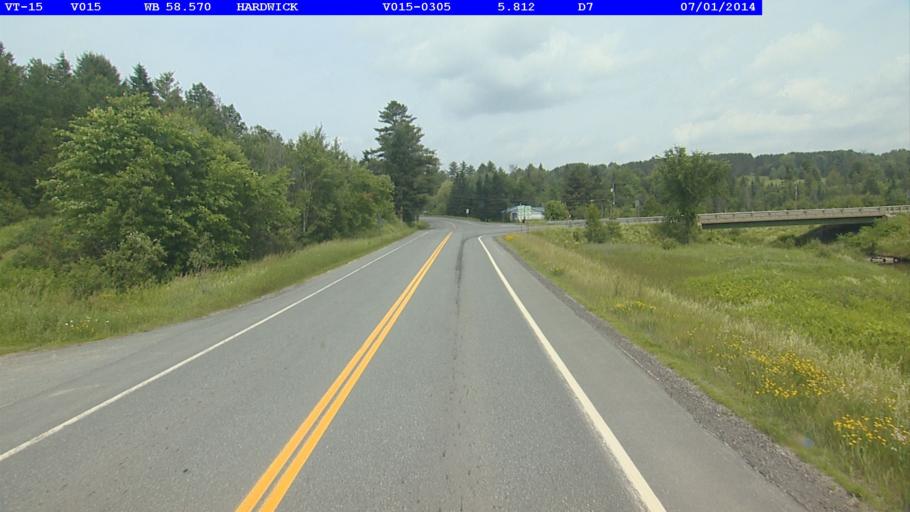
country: US
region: Vermont
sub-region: Caledonia County
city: Hardwick
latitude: 44.4989
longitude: -72.3232
